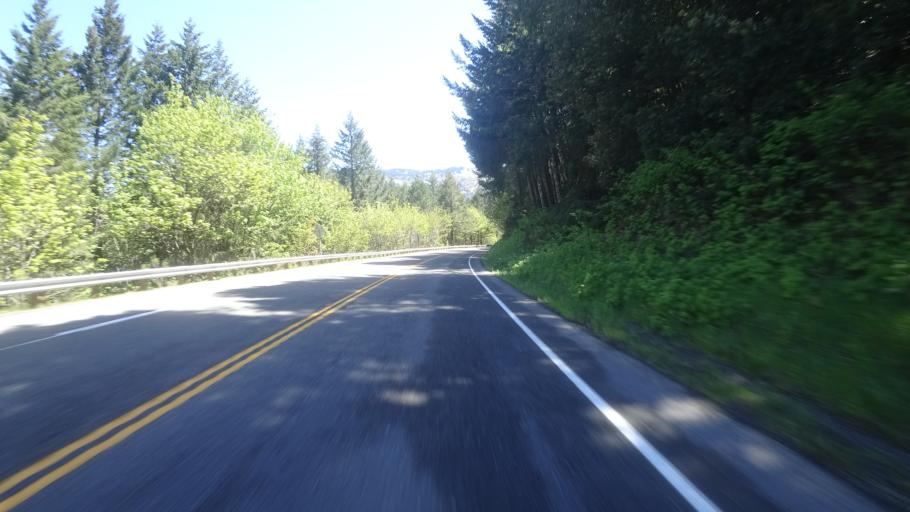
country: US
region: California
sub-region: Humboldt County
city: Blue Lake
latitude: 40.9054
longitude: -123.8227
